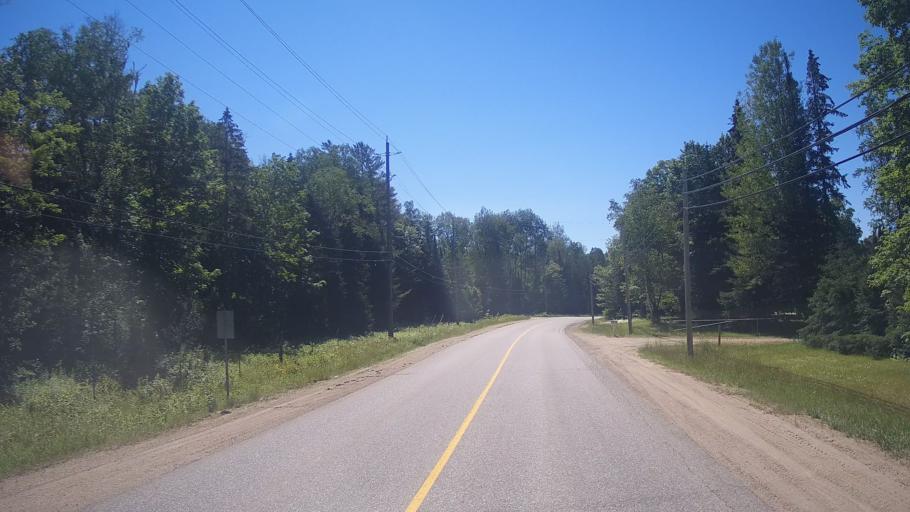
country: CA
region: Ontario
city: Huntsville
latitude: 45.3714
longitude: -79.2077
